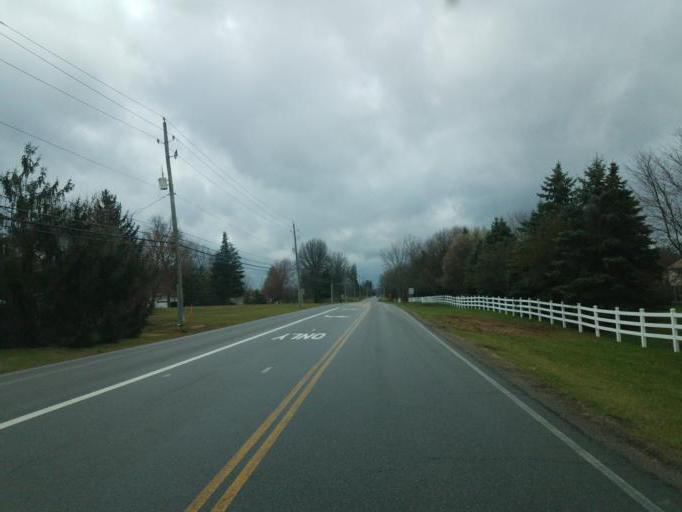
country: US
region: Ohio
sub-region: Franklin County
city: Westerville
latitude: 40.1717
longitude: -82.9345
